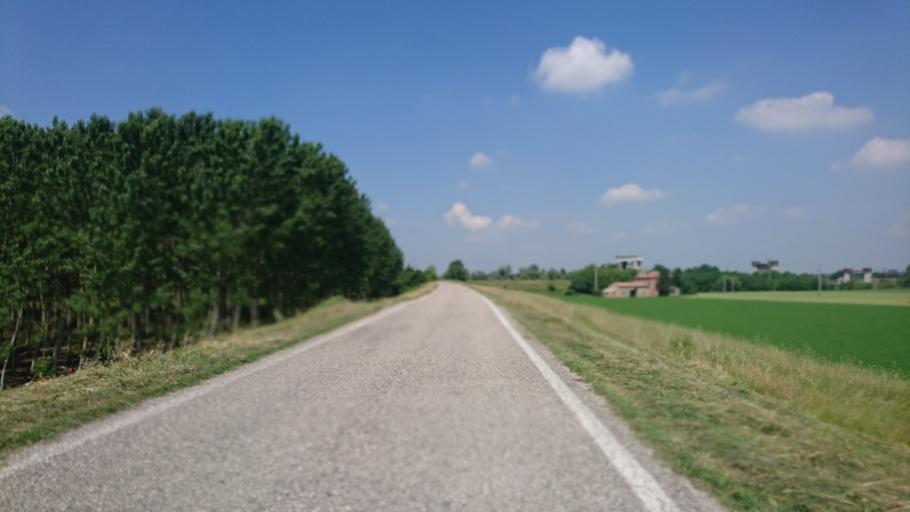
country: IT
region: Lombardy
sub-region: Provincia di Mantova
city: Sustinente
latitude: 45.0743
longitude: 10.9812
